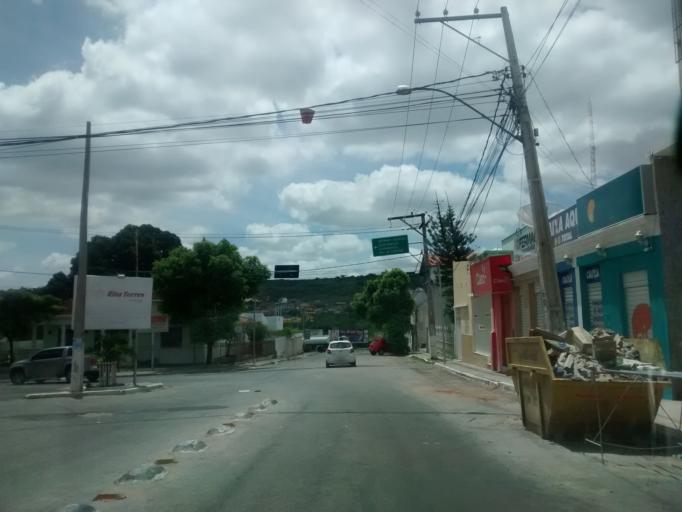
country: BR
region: Bahia
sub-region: Brumado
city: Brumado
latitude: -14.2054
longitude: -41.6650
